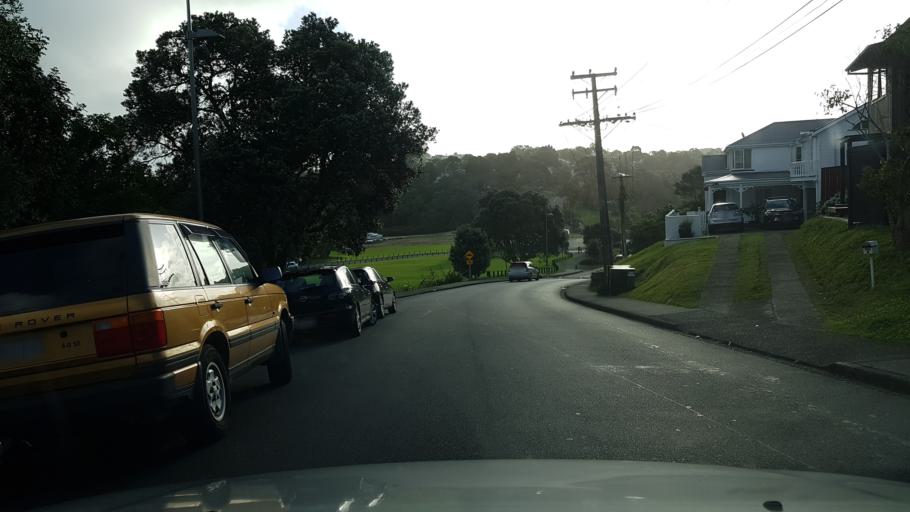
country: NZ
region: Auckland
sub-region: Auckland
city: North Shore
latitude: -36.8151
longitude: 174.7424
